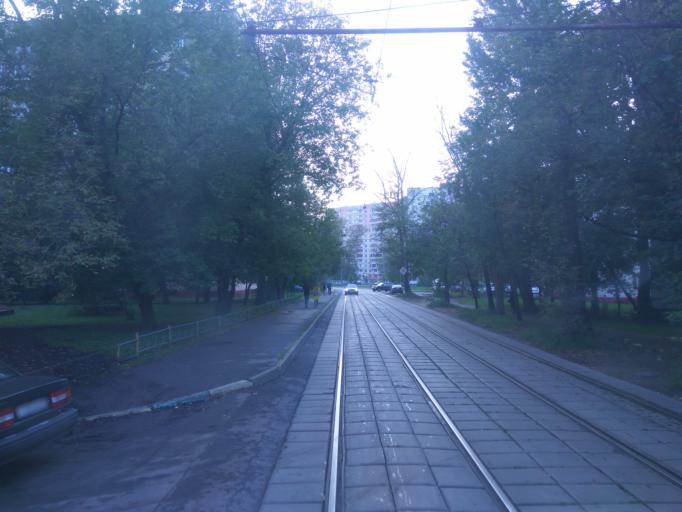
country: RU
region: Moskovskaya
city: Bogorodskoye
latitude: 55.8186
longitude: 37.7154
